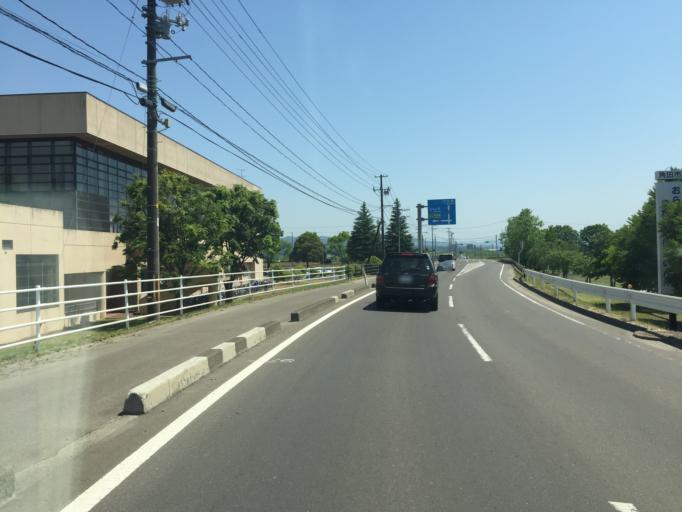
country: JP
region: Miyagi
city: Kakuda
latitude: 37.9698
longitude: 140.8042
